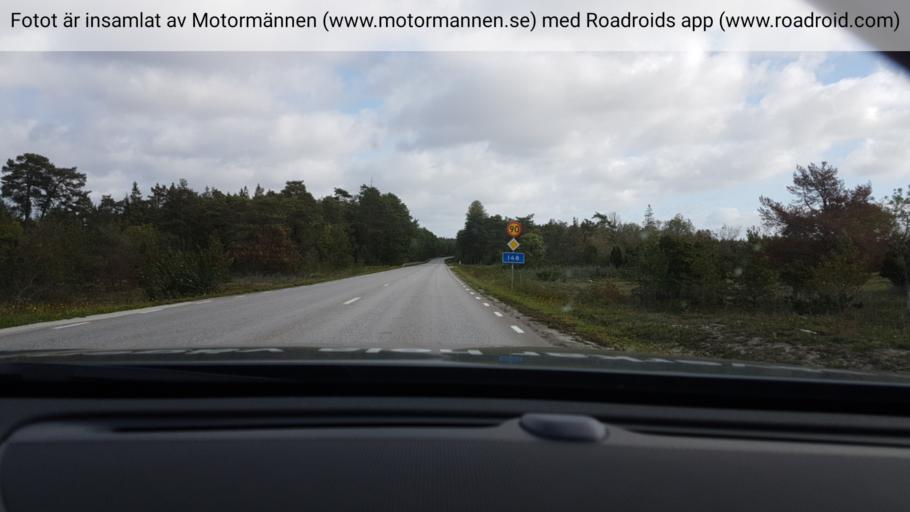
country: SE
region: Gotland
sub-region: Gotland
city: Slite
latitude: 57.8517
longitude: 18.9818
